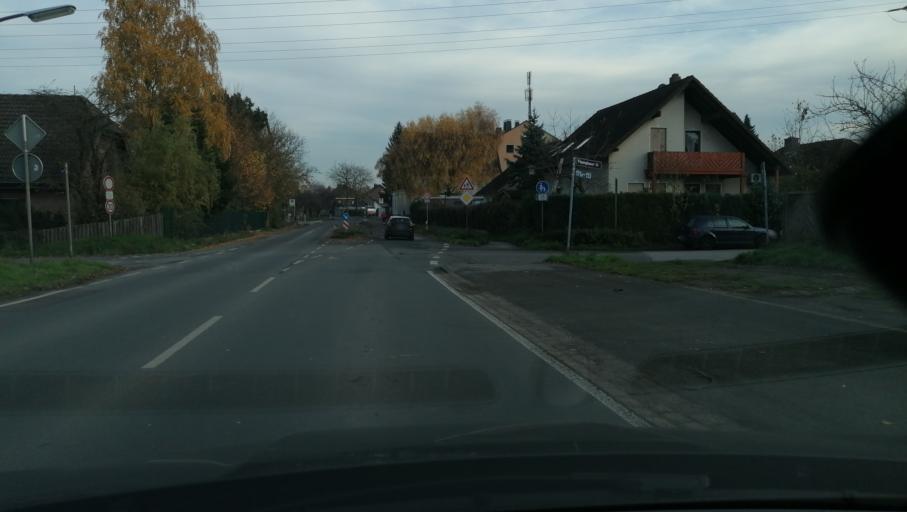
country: DE
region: North Rhine-Westphalia
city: Castrop-Rauxel
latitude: 51.5789
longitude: 7.2630
